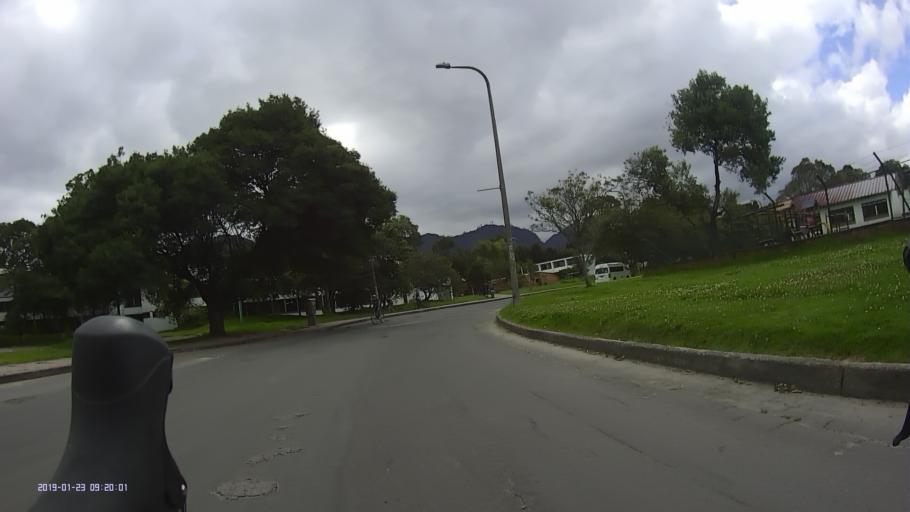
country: CO
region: Bogota D.C.
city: Bogota
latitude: 4.6421
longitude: -74.0827
